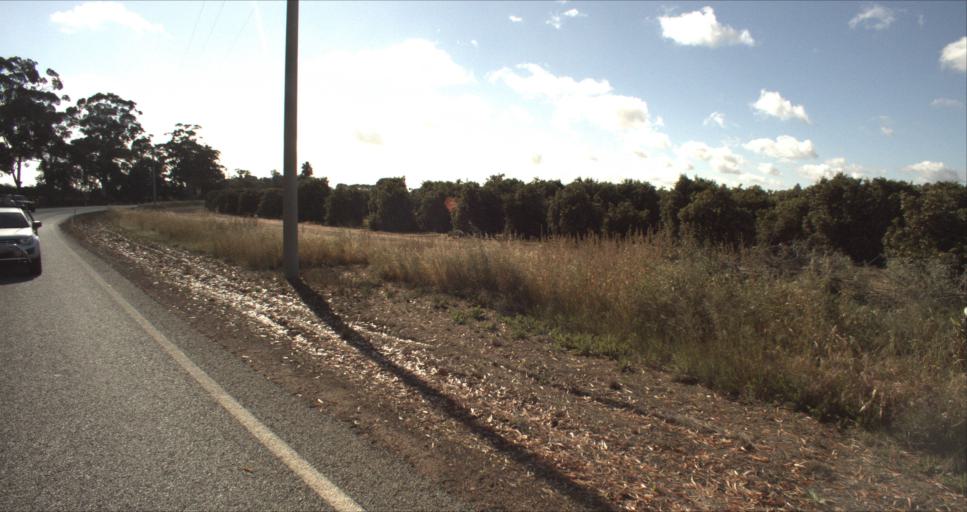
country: AU
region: New South Wales
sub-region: Leeton
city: Leeton
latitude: -34.5439
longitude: 146.3316
